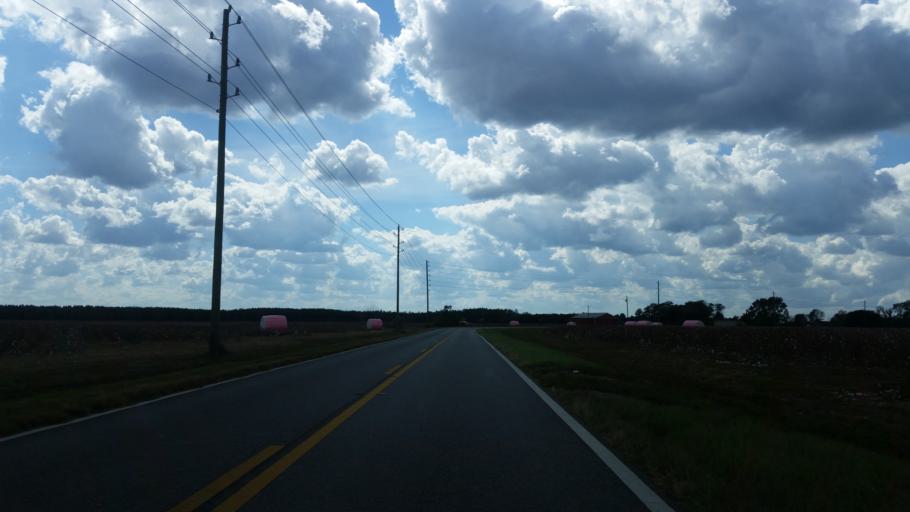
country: US
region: Alabama
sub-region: Escambia County
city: Atmore
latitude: 30.8904
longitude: -87.4796
